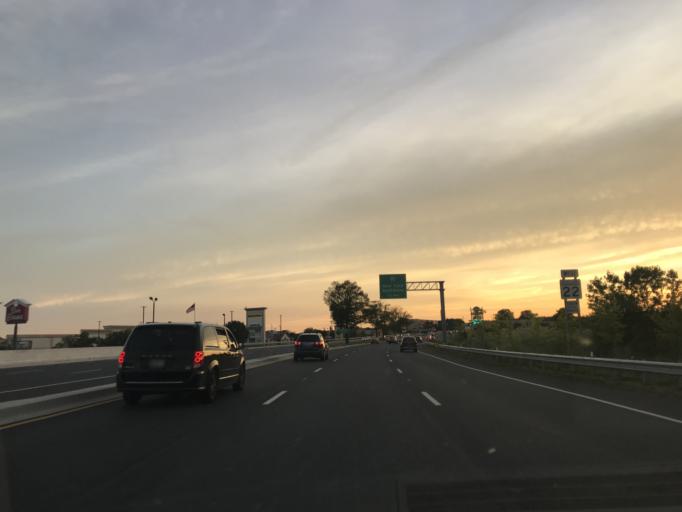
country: US
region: Maryland
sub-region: Harford County
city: Aberdeen
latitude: 39.5226
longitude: -76.1795
